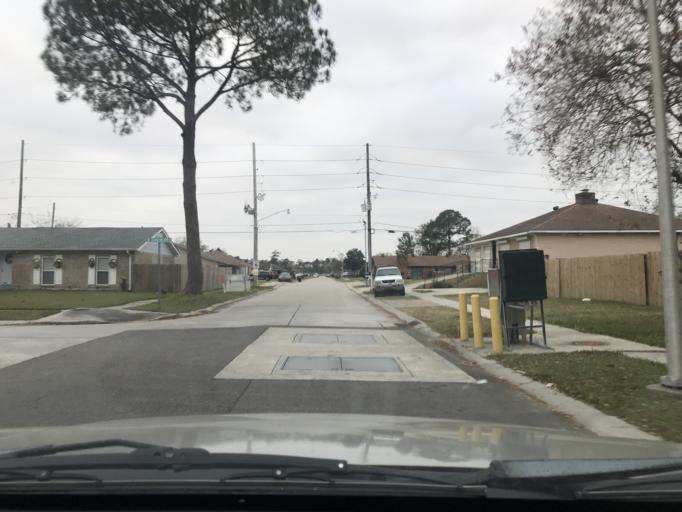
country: US
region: Louisiana
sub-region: Jefferson Parish
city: Woodmere
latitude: 29.8623
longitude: -90.0809
